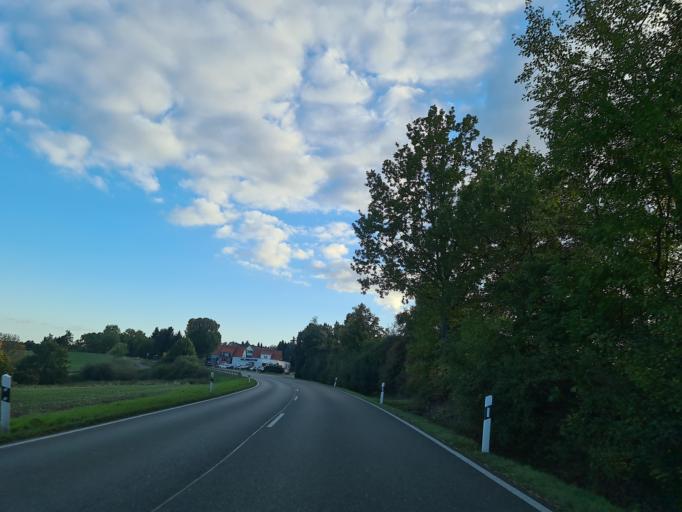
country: DE
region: Thuringia
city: Teichwitz
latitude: 50.7424
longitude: 12.0862
